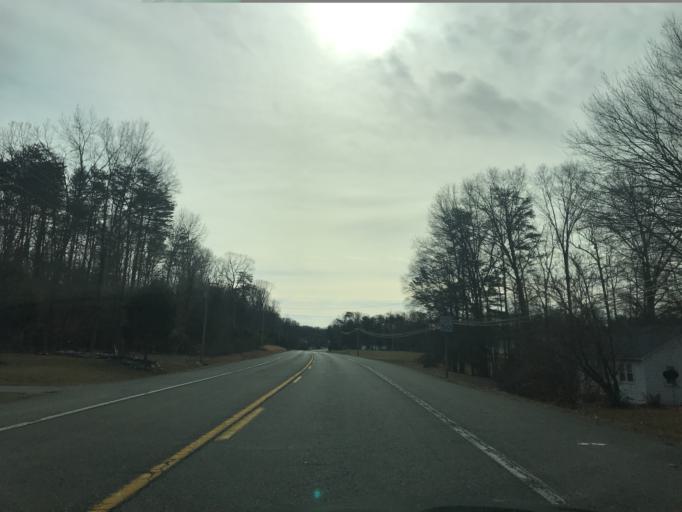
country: US
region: Virginia
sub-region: Prince William County
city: Quantico Station
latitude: 38.4661
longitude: -77.2206
